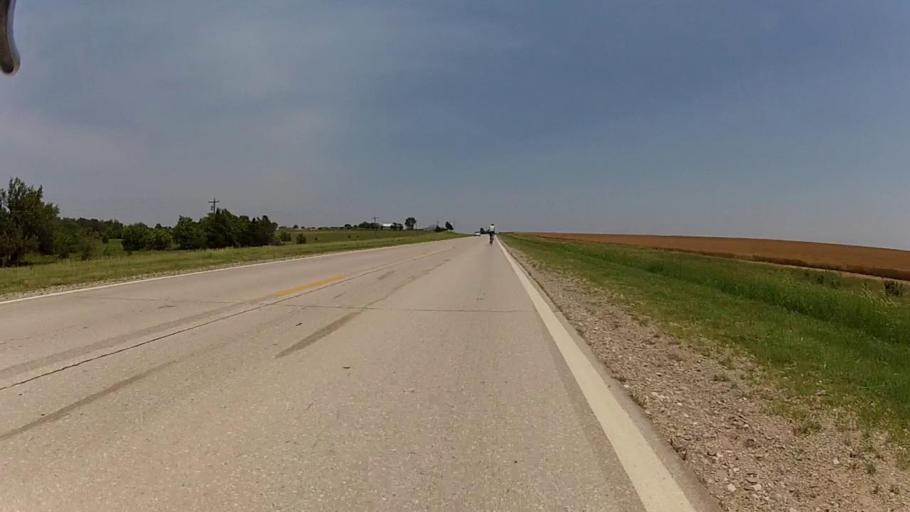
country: US
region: Kansas
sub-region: Sumner County
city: Wellington
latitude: 37.0568
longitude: -97.3090
